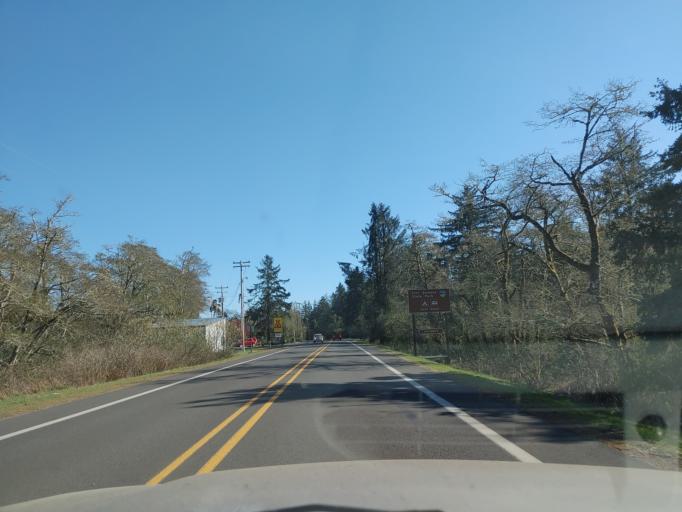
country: US
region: Oregon
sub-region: Clatsop County
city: Warrenton
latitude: 46.1858
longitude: -123.9569
